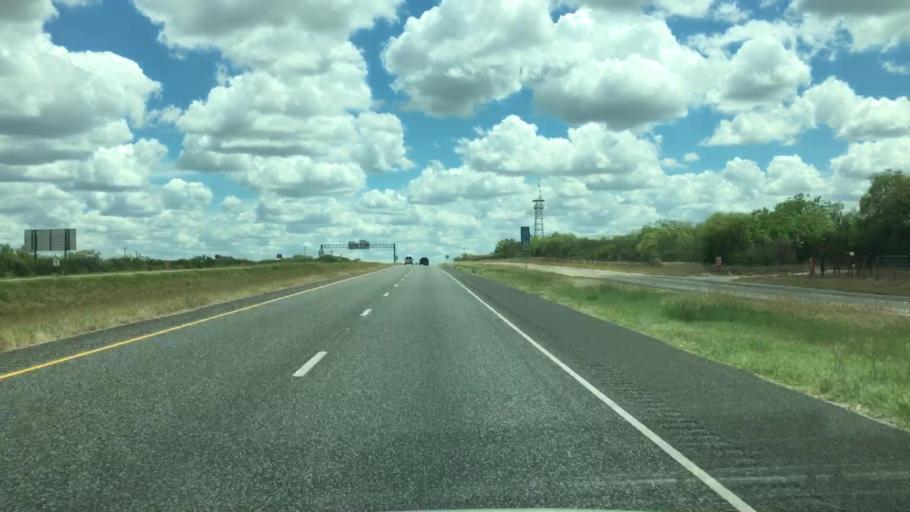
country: US
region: Texas
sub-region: Atascosa County
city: Pleasanton
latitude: 28.9038
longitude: -98.4265
